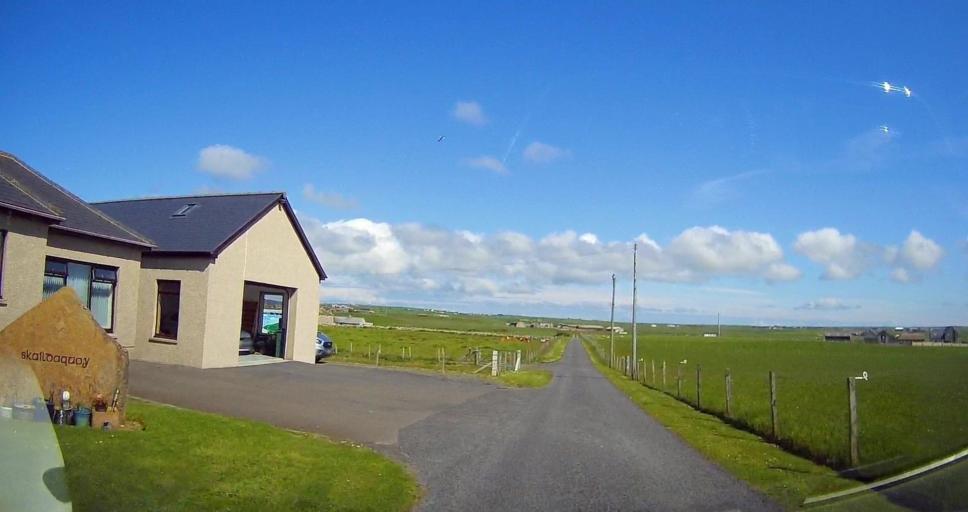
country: GB
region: Scotland
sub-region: Orkney Islands
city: Kirkwall
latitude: 58.8977
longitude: -2.9293
